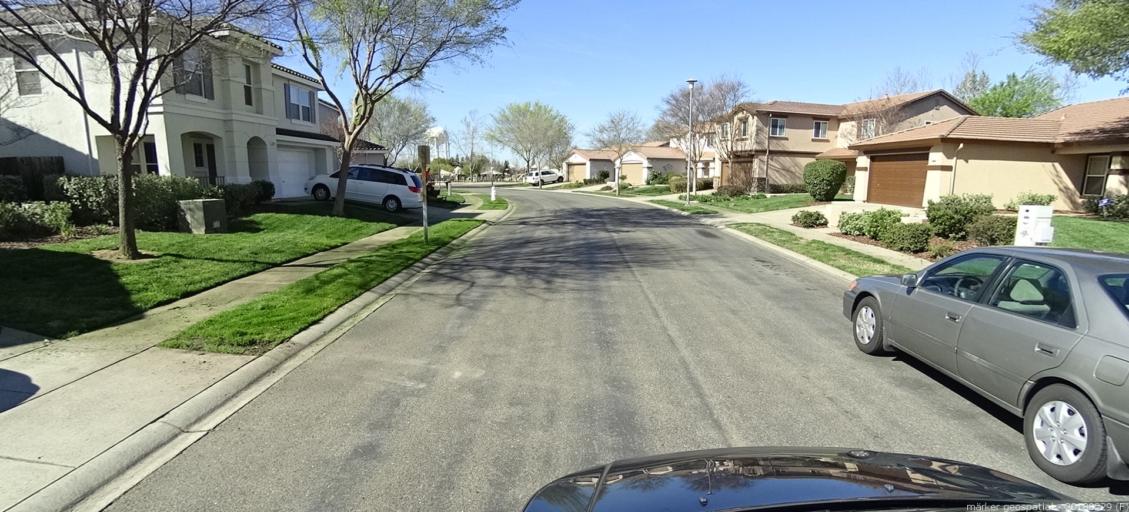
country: US
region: California
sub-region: Sacramento County
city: Rancho Cordova
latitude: 38.5463
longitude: -121.2760
